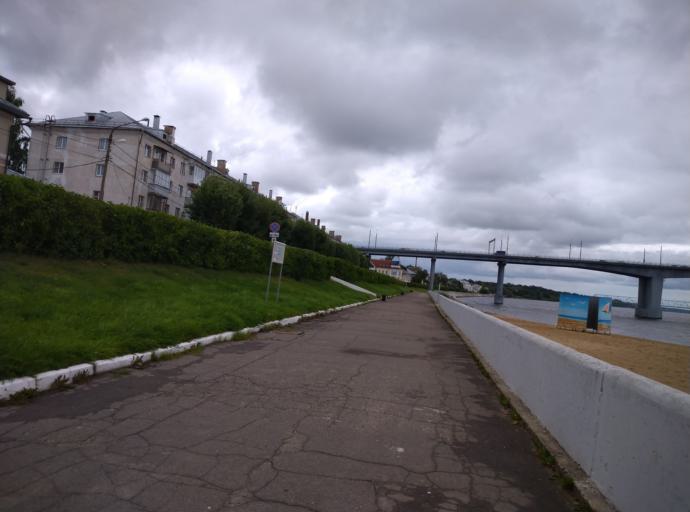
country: RU
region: Kostroma
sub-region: Kostromskoy Rayon
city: Kostroma
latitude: 57.7572
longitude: 40.9399
